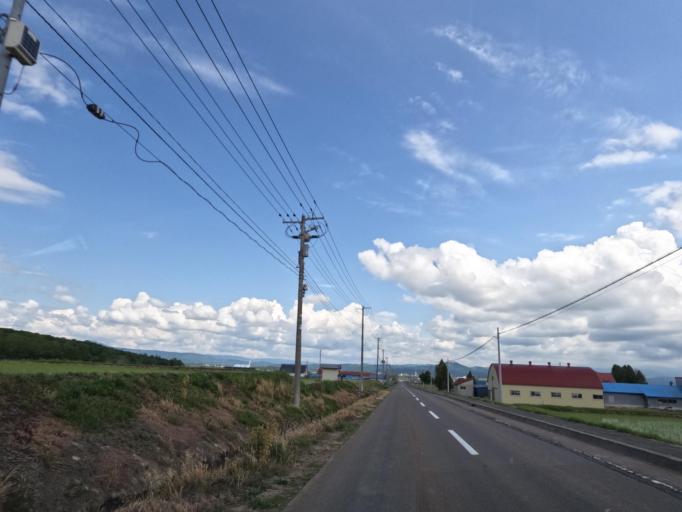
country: JP
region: Hokkaido
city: Takikawa
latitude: 43.5762
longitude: 141.8479
